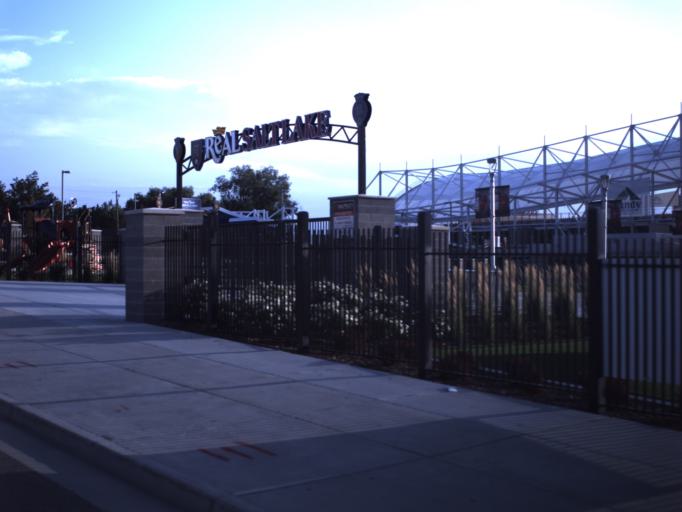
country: US
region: Utah
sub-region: Salt Lake County
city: Sandy City
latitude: 40.5838
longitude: -111.8910
